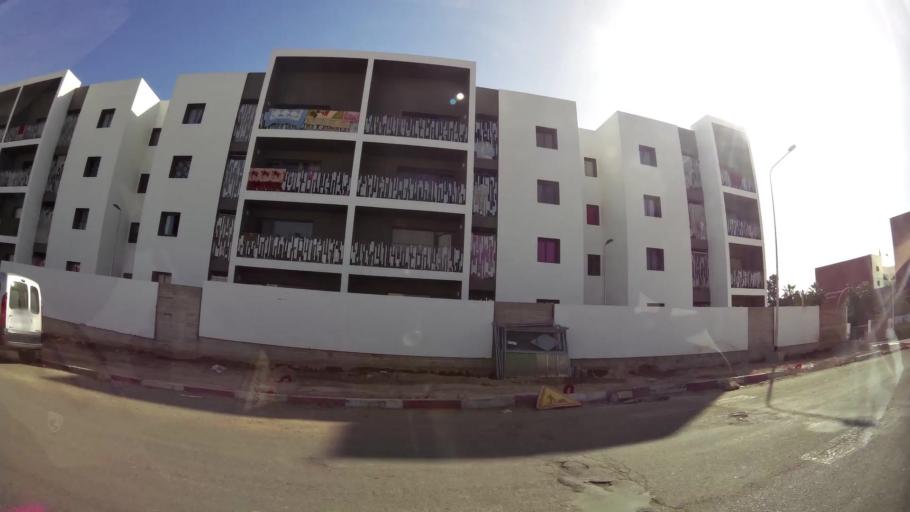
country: MA
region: Oued ed Dahab-Lagouira
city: Dakhla
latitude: 30.4208
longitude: -9.5738
